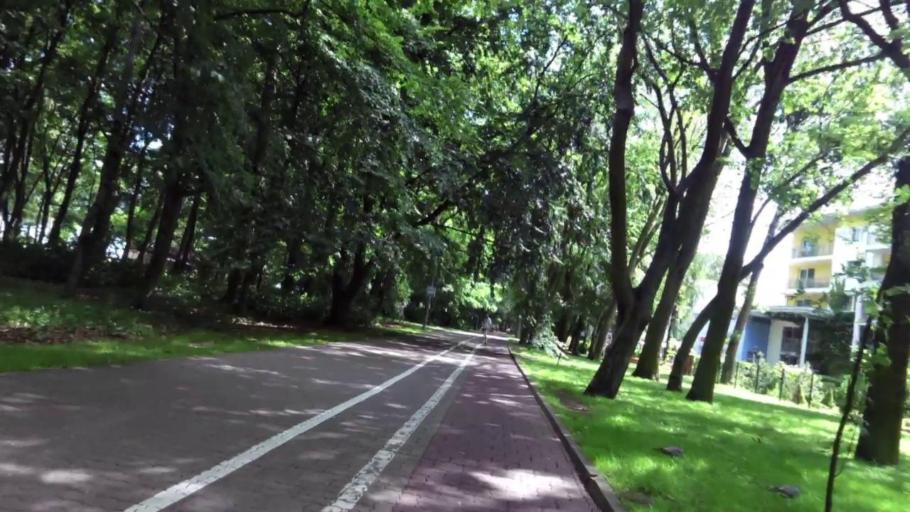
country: PL
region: West Pomeranian Voivodeship
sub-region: Powiat kolobrzeski
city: Kolobrzeg
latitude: 54.1865
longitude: 15.5885
